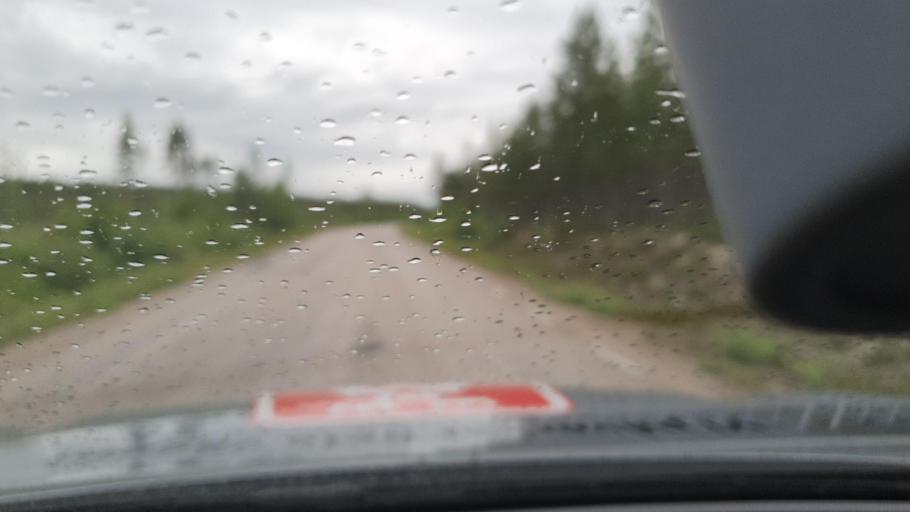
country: SE
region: Norrbotten
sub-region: Overkalix Kommun
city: OEverkalix
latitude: 66.3783
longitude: 22.7953
